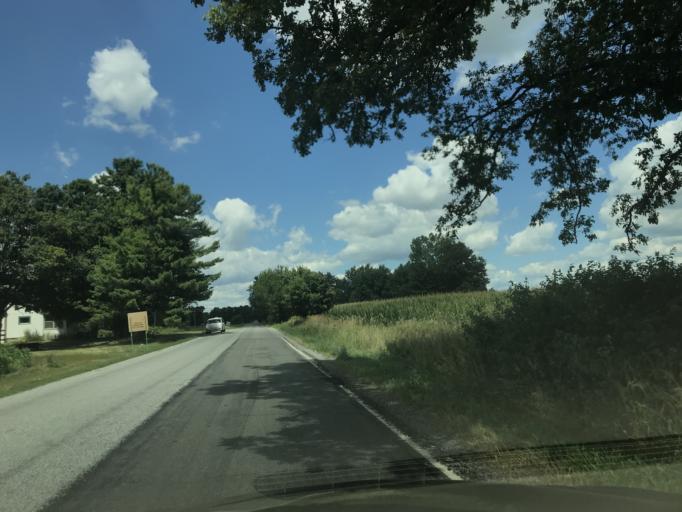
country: US
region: Michigan
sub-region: Ingham County
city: Holt
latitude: 42.5990
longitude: -84.5624
